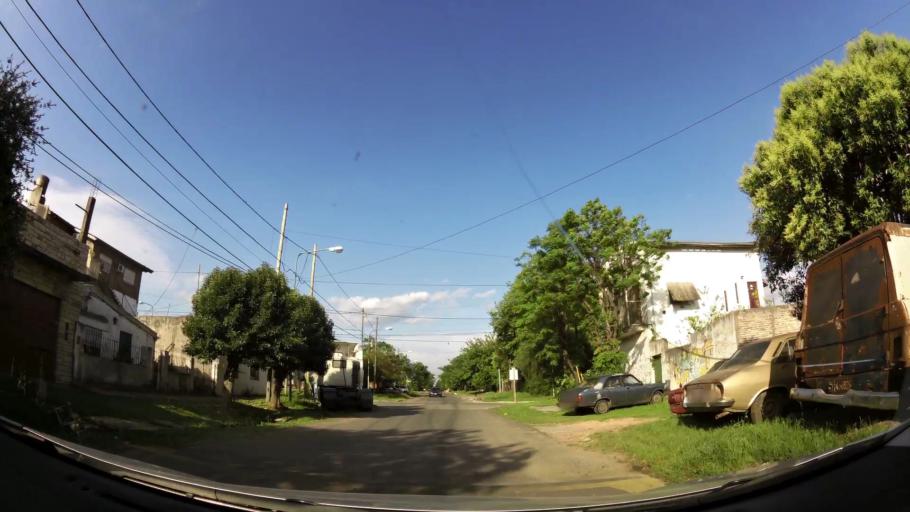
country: AR
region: Buenos Aires
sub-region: Partido de Tigre
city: Tigre
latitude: -34.4698
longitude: -58.6630
